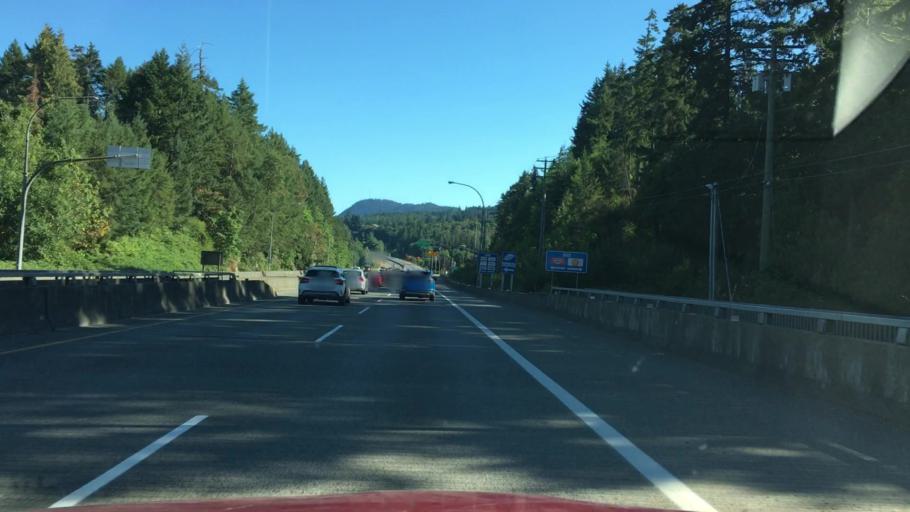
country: CA
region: British Columbia
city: North Saanich
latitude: 48.6559
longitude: -123.5609
